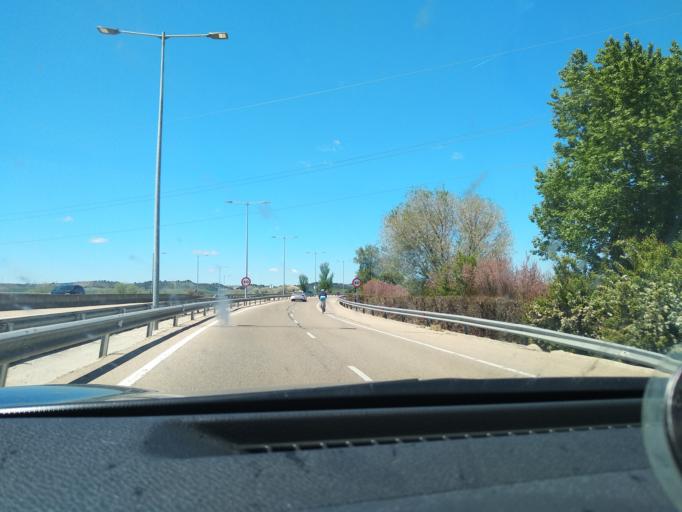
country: ES
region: Castille and Leon
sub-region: Provincia de Valladolid
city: Zaratan
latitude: 41.6432
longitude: -4.7648
